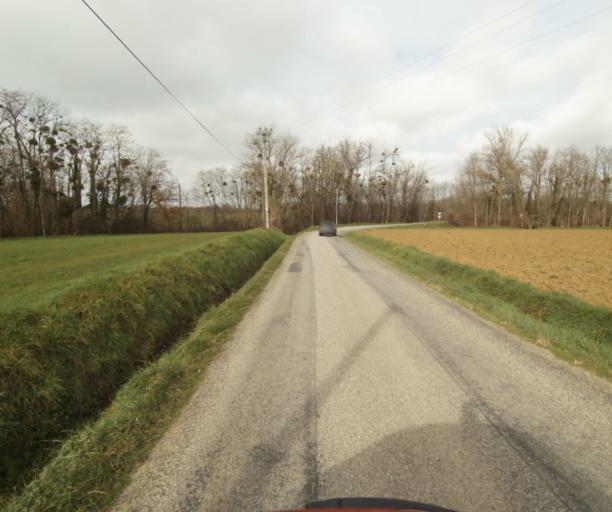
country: FR
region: Midi-Pyrenees
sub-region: Departement de l'Ariege
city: Pamiers
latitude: 43.1060
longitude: 1.5483
